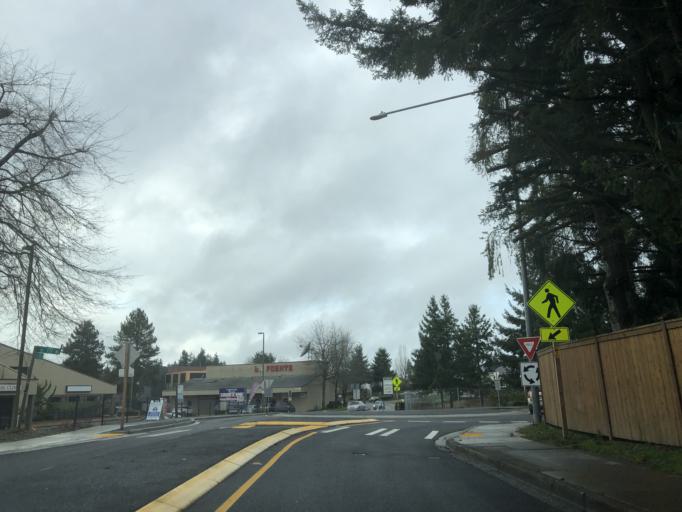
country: US
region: Washington
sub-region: King County
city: Fairwood
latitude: 47.4450
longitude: -122.1476
